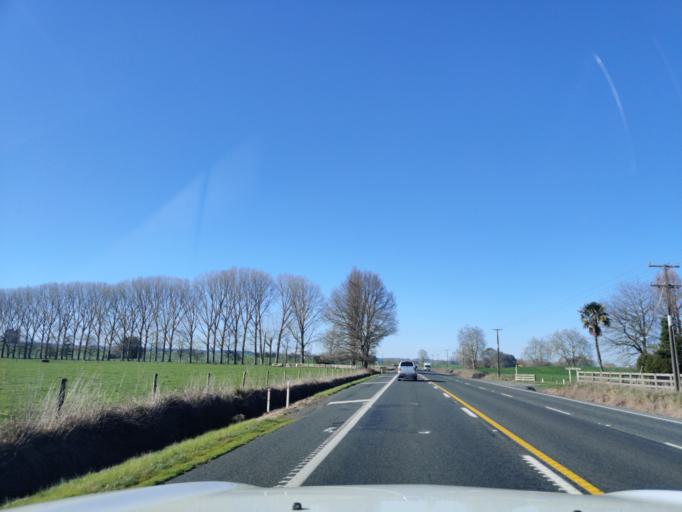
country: NZ
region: Waikato
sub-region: Matamata-Piako District
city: Matamata
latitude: -38.0176
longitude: 175.7802
